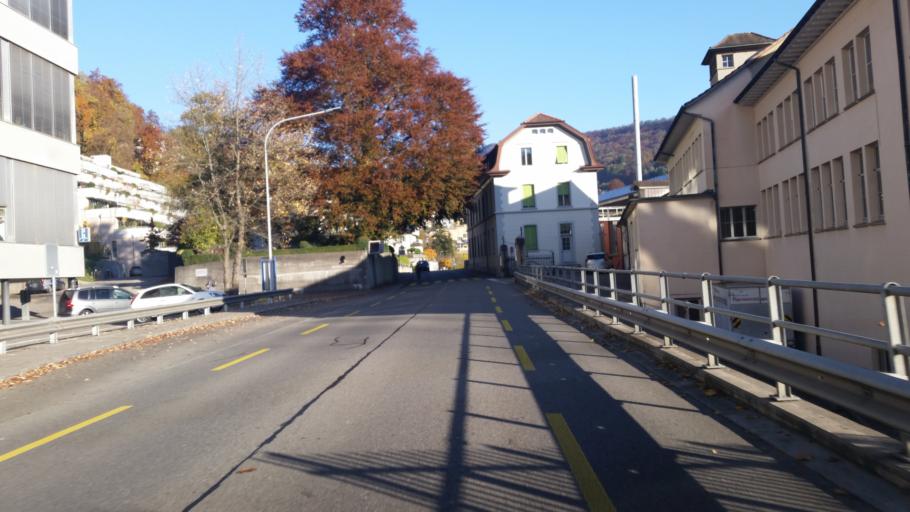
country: CH
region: Aargau
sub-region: Bezirk Baden
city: Baden
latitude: 47.4827
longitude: 8.3092
